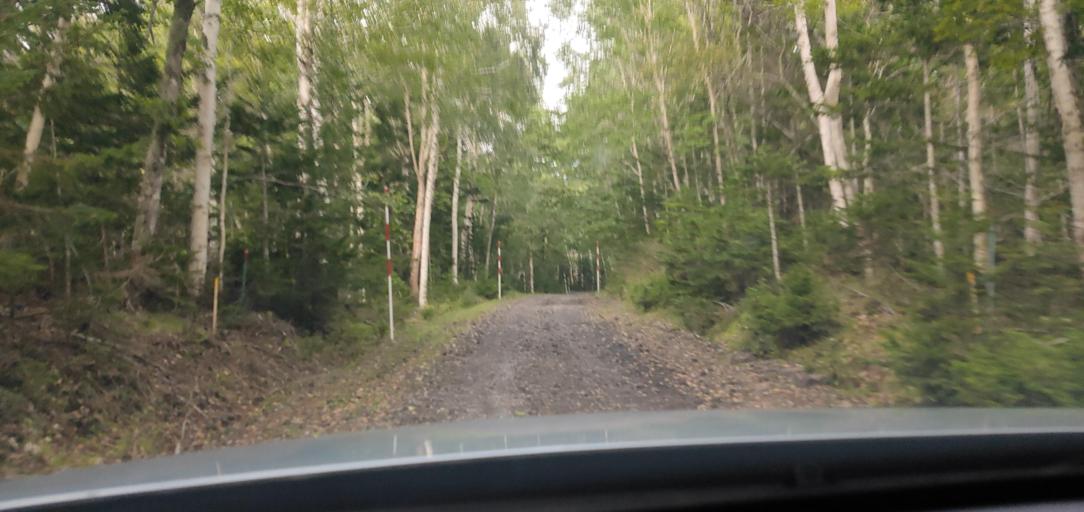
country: JP
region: Hokkaido
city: Kitami
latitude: 43.3737
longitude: 143.9658
